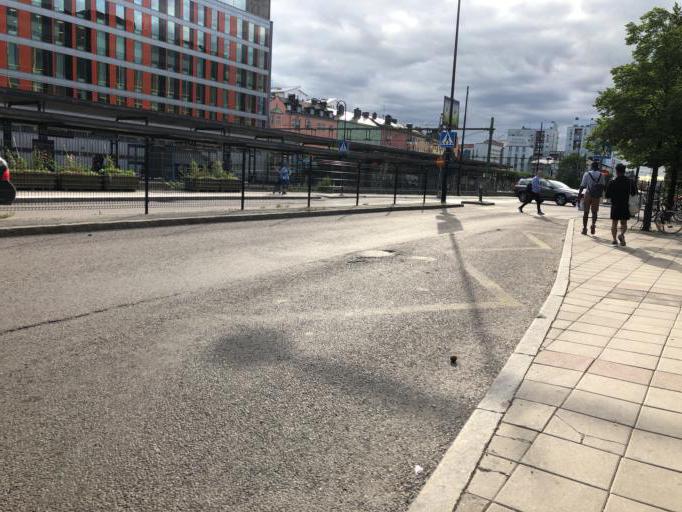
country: SE
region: Stockholm
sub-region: Sundbybergs Kommun
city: Sundbyberg
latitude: 59.3608
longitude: 17.9724
